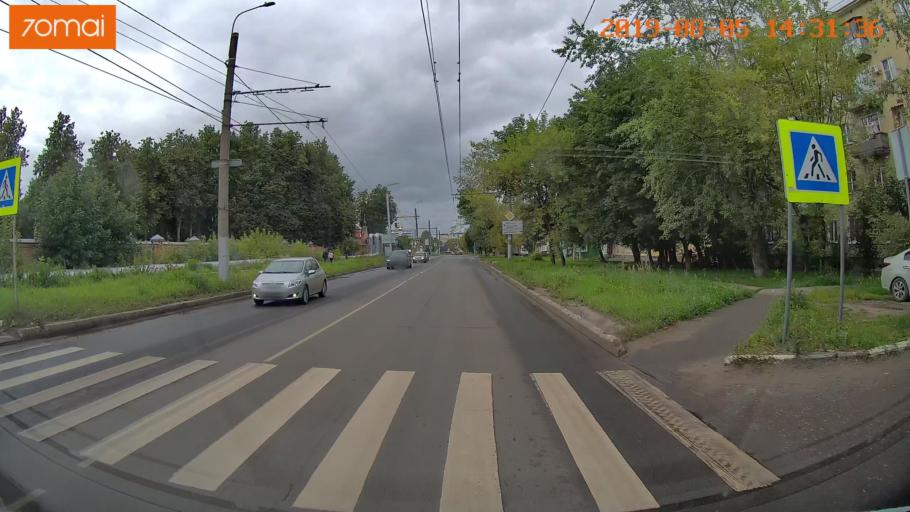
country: RU
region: Ivanovo
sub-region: Gorod Ivanovo
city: Ivanovo
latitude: 56.9877
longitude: 40.9997
